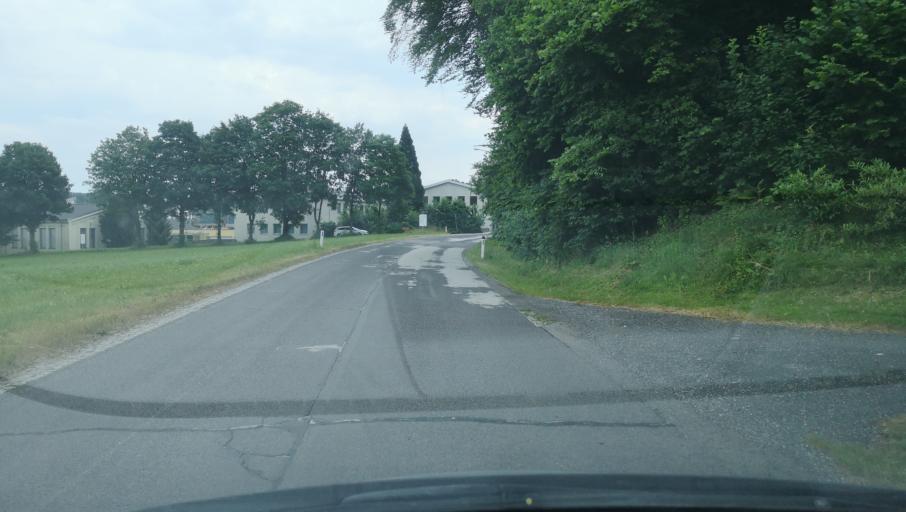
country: AT
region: Lower Austria
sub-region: Politischer Bezirk Melk
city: Ybbs an der Donau
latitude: 48.1897
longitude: 15.0625
